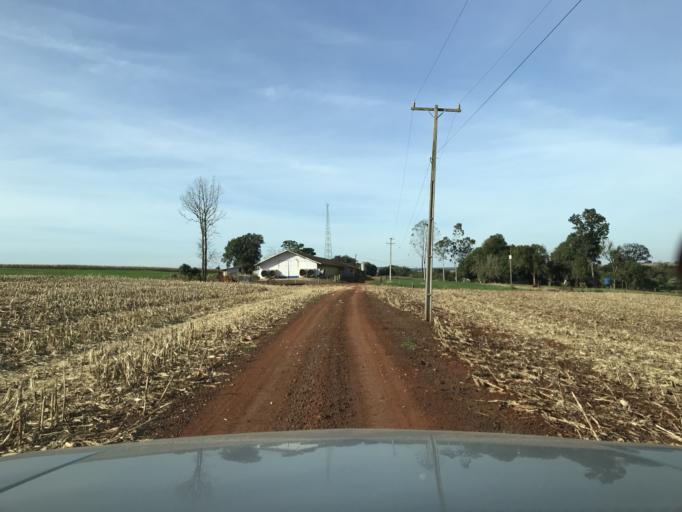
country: BR
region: Parana
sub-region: Palotina
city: Palotina
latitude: -24.2484
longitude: -53.7478
